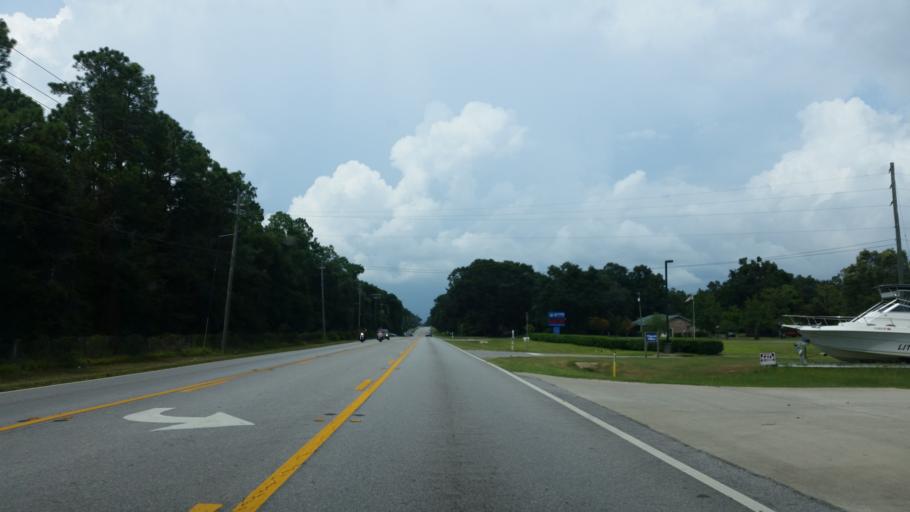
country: US
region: Florida
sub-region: Santa Rosa County
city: Pace
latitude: 30.6149
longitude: -87.1820
